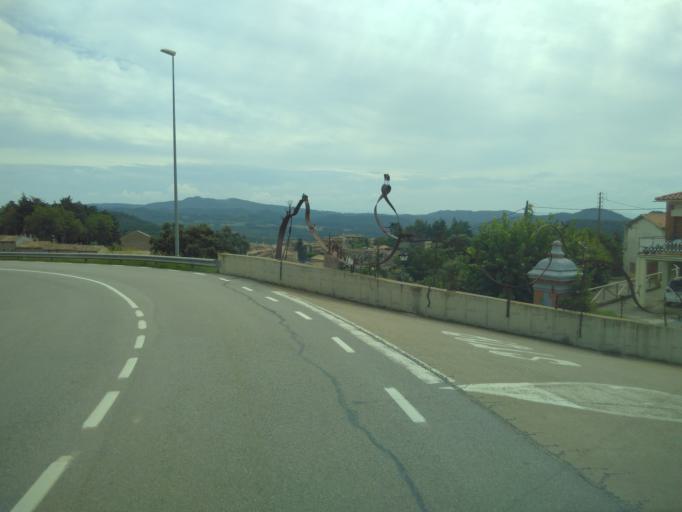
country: ES
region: Catalonia
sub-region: Provincia de Barcelona
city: Alpens
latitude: 42.1212
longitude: 2.0992
